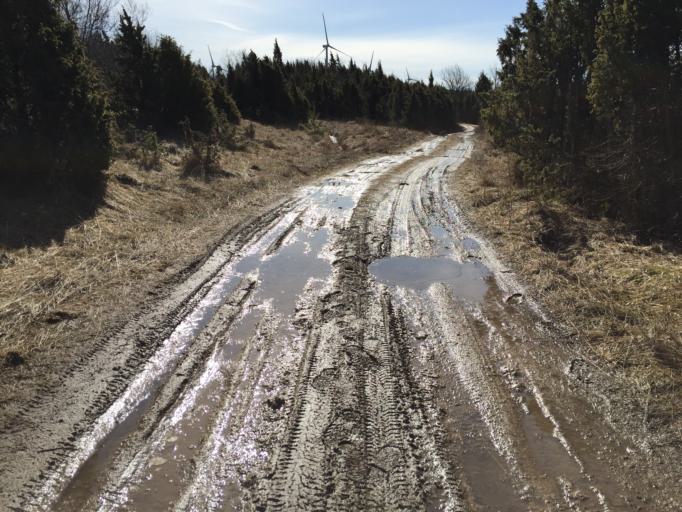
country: EE
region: Laeaene
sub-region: Haapsalu linn
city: Haapsalu
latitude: 58.6474
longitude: 23.5111
